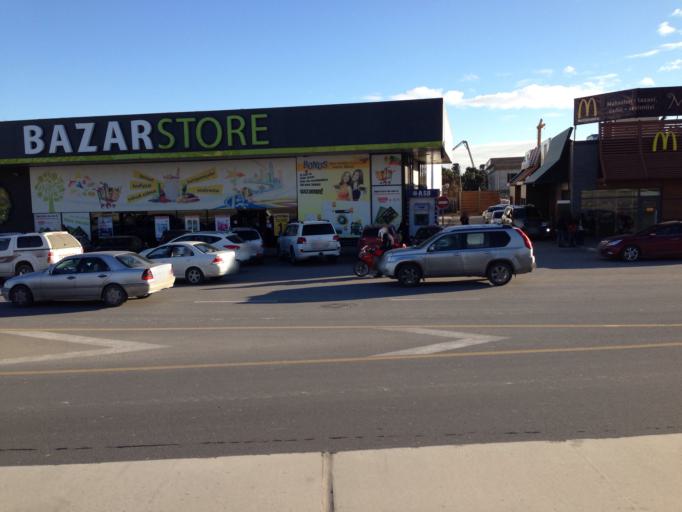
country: AZ
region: Baki
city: Baku
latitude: 40.4000
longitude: 49.8499
